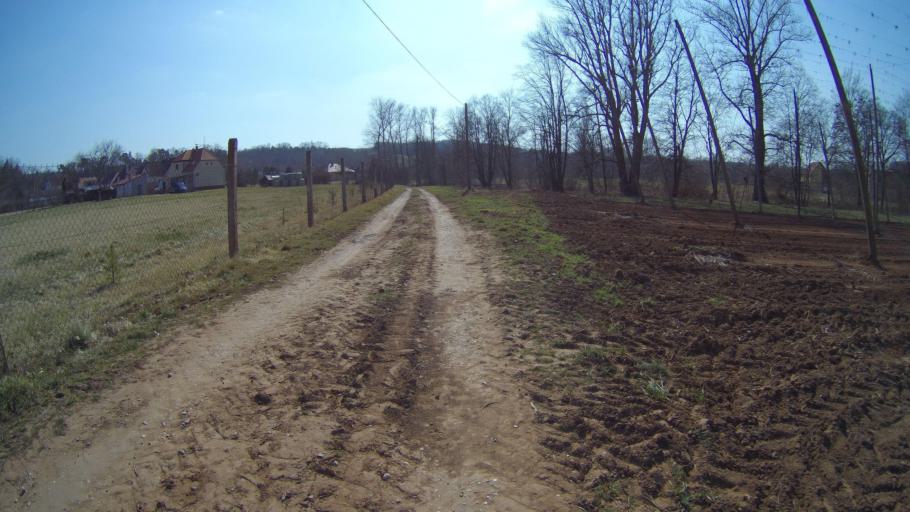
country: CZ
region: Ustecky
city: Mecholupy
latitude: 50.2754
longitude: 13.5654
